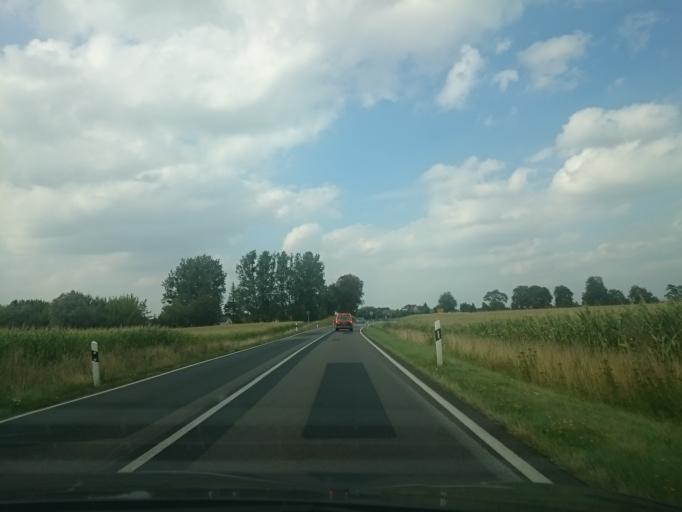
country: DE
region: Mecklenburg-Vorpommern
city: Ferdinandshof
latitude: 53.6595
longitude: 13.9011
